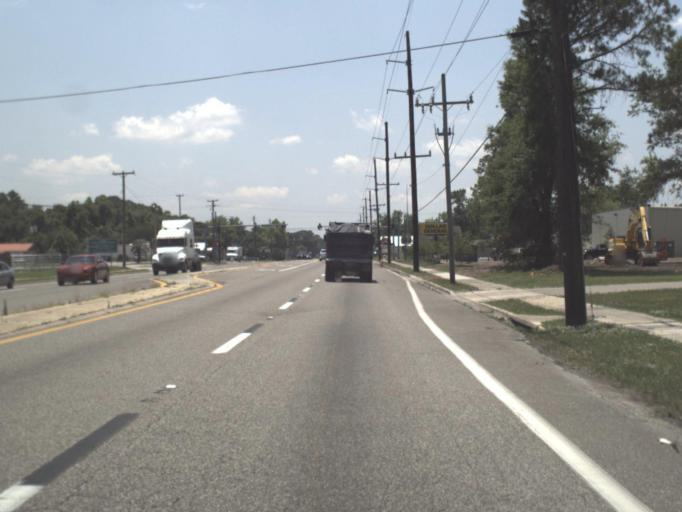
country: US
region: Florida
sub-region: Bradford County
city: Starke
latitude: 29.9681
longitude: -82.1030
